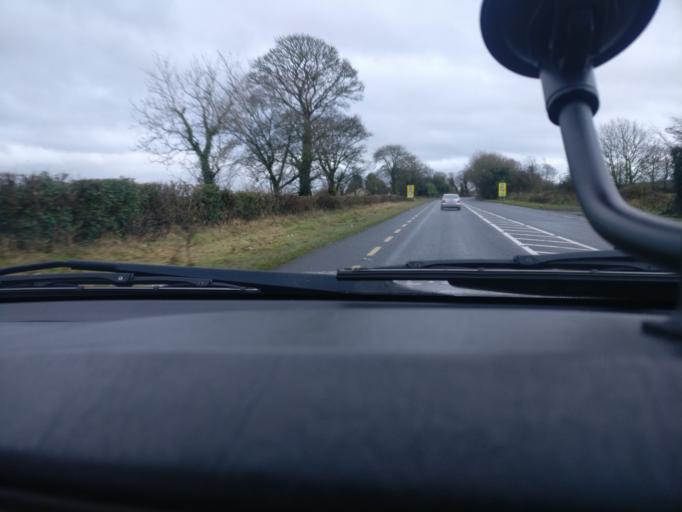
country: IE
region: Leinster
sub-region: Kildare
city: Kilcock
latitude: 53.4215
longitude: -6.7435
